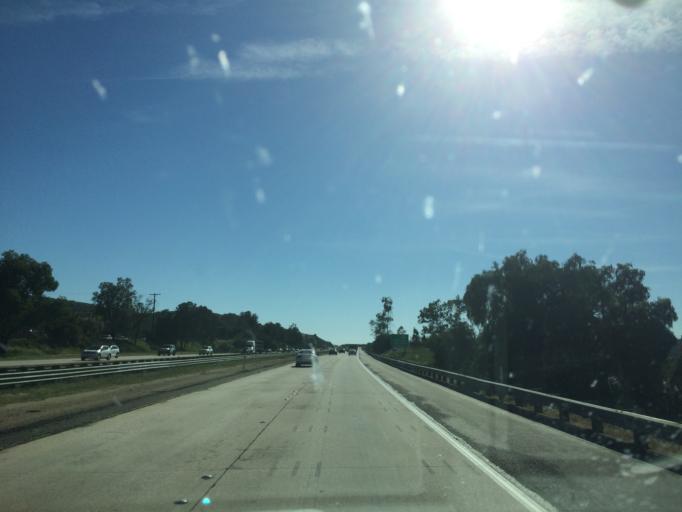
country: US
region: California
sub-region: San Diego County
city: Granite Hills
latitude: 32.8314
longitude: -116.8975
